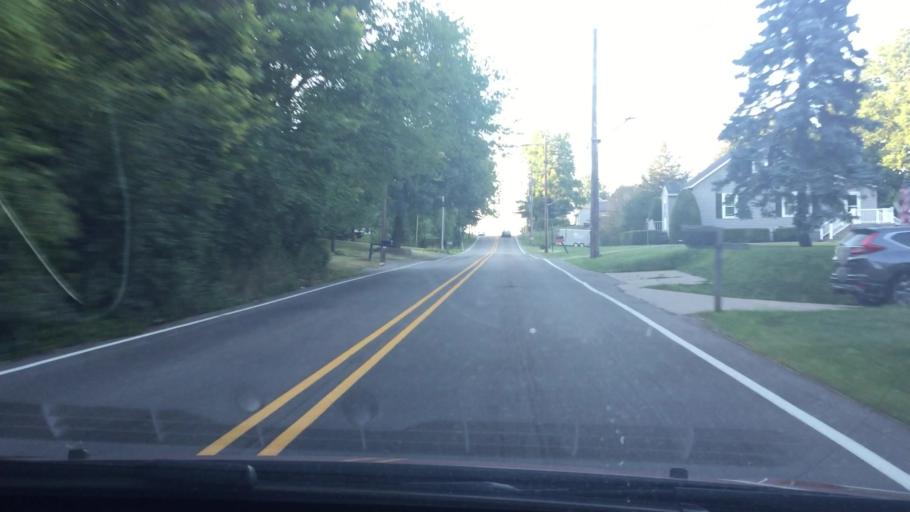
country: US
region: Iowa
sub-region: Muscatine County
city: Muscatine
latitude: 41.4288
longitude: -91.0649
